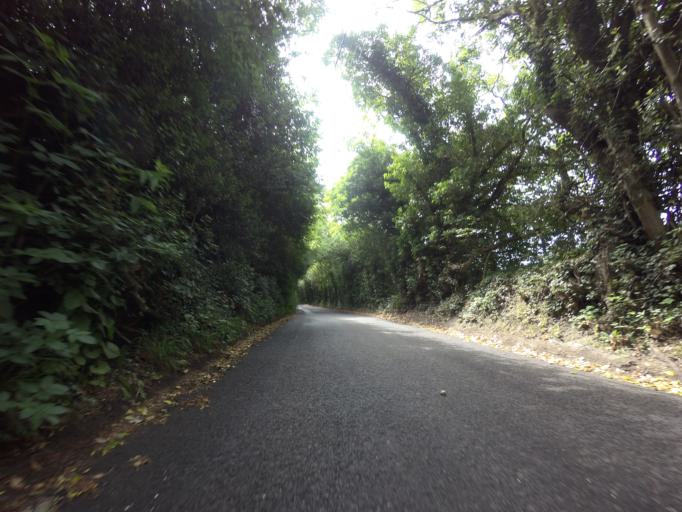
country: GB
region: England
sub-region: Kent
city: Halstead
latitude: 51.3529
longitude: 0.1387
